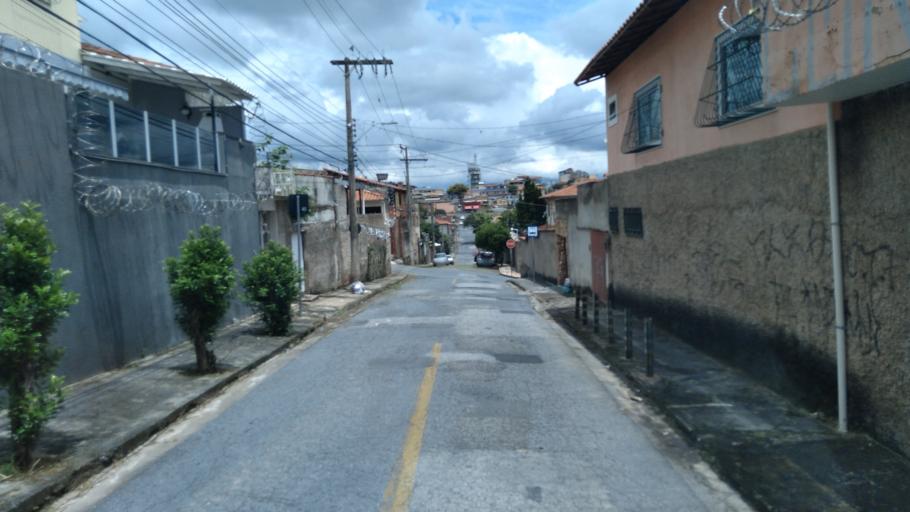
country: BR
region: Minas Gerais
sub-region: Belo Horizonte
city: Belo Horizonte
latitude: -19.9224
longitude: -43.9011
